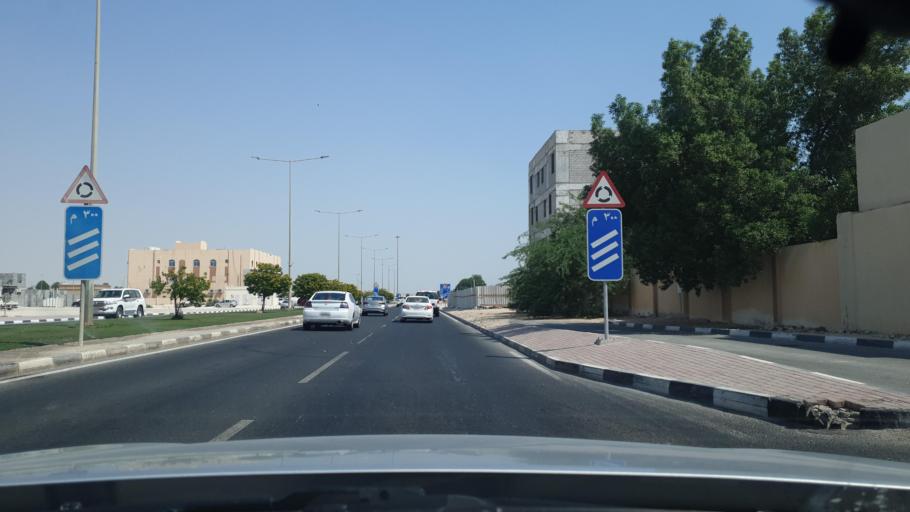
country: QA
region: Al Khawr
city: Al Khawr
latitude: 25.6889
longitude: 51.4974
